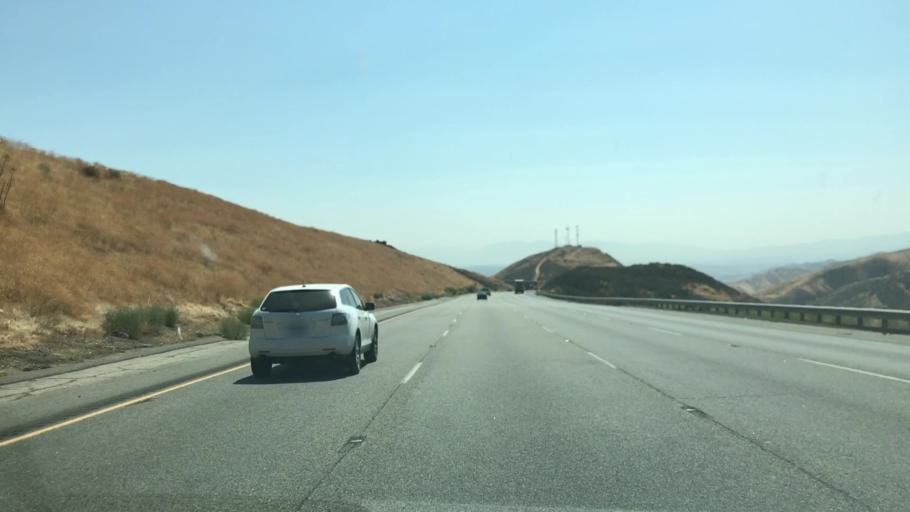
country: US
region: California
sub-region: Los Angeles County
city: Castaic
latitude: 34.5589
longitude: -118.6778
